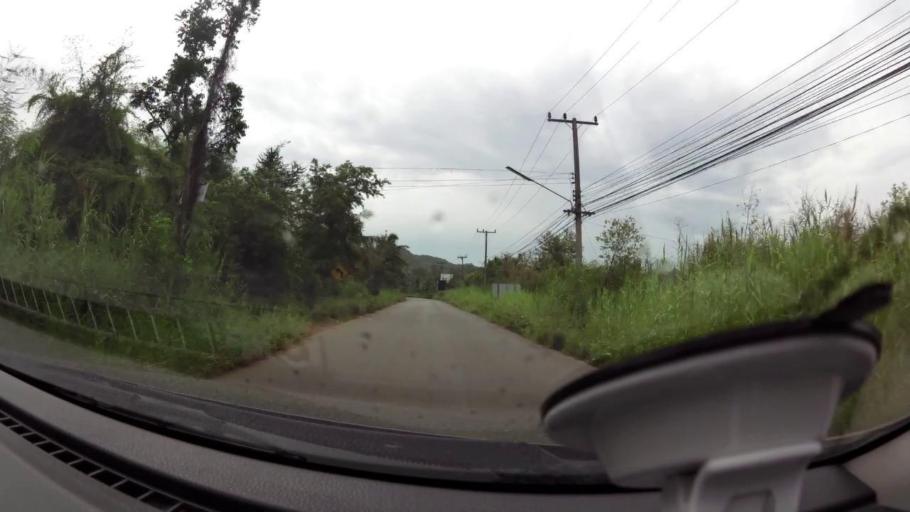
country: TH
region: Prachuap Khiri Khan
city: Pran Buri
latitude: 12.4460
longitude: 99.9669
